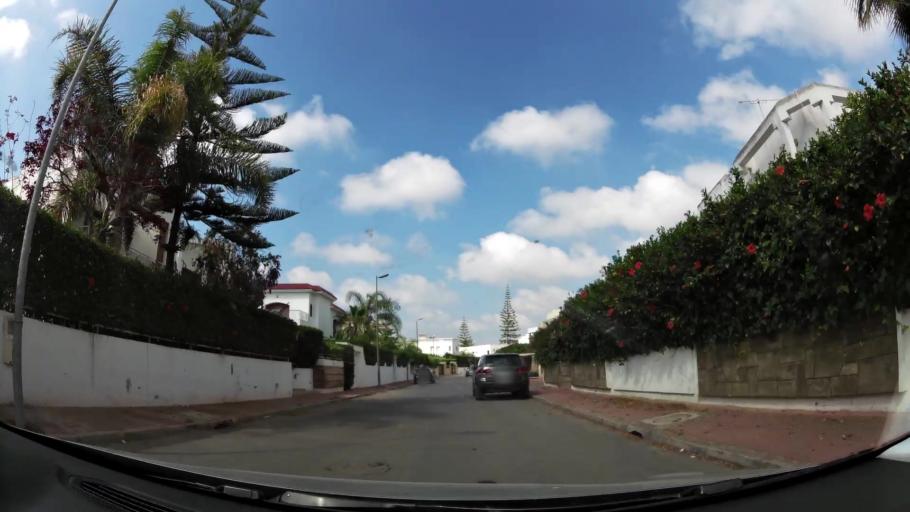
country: MA
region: Rabat-Sale-Zemmour-Zaer
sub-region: Skhirate-Temara
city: Temara
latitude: 33.9632
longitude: -6.8636
